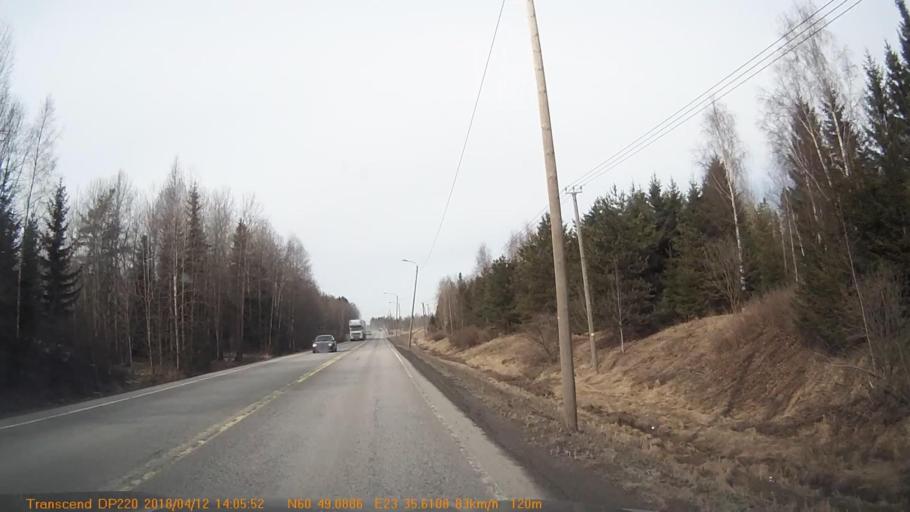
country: FI
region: Haeme
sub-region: Forssa
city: Forssa
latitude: 60.8184
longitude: 23.5933
